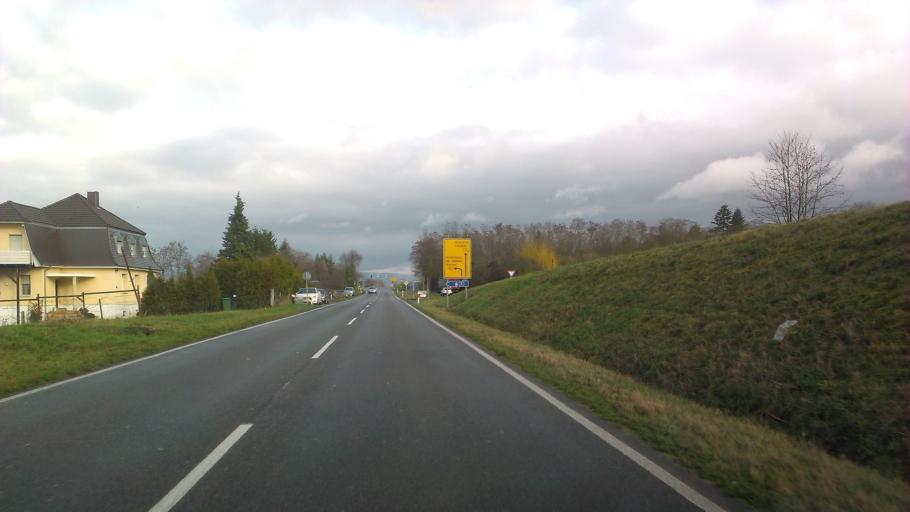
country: DE
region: Baden-Wuerttemberg
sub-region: Karlsruhe Region
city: Bruchsal
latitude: 49.1397
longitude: 8.6069
